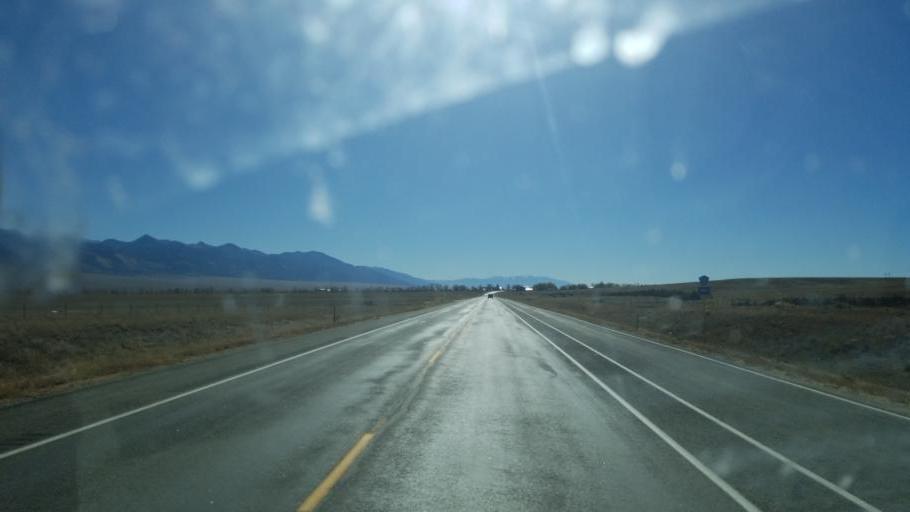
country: US
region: Colorado
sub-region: Saguache County
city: Saguache
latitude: 38.2601
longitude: -105.9577
